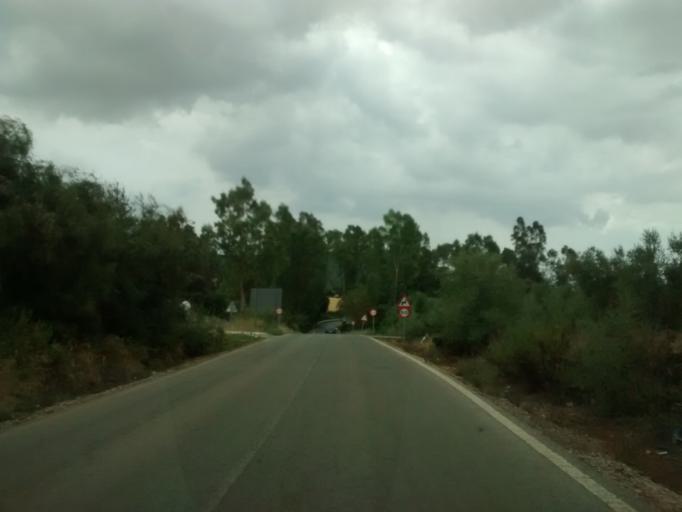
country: ES
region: Andalusia
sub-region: Provincia de Cadiz
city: Puerto Serrano
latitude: 36.8803
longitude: -5.5745
